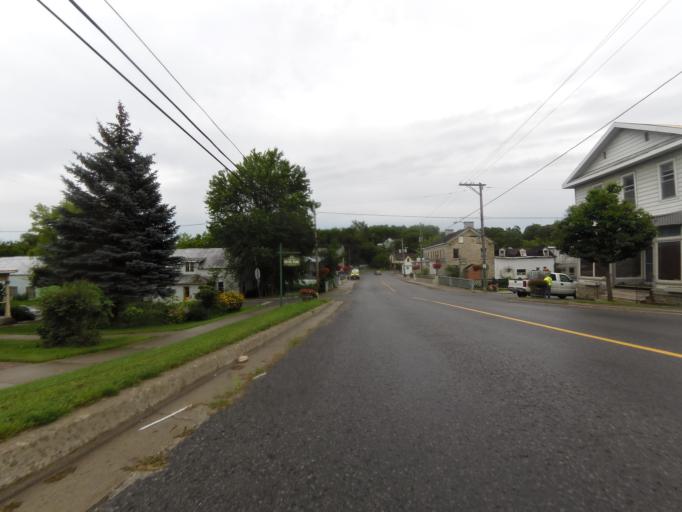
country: CA
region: Ontario
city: Perth
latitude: 45.0169
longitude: -76.3637
